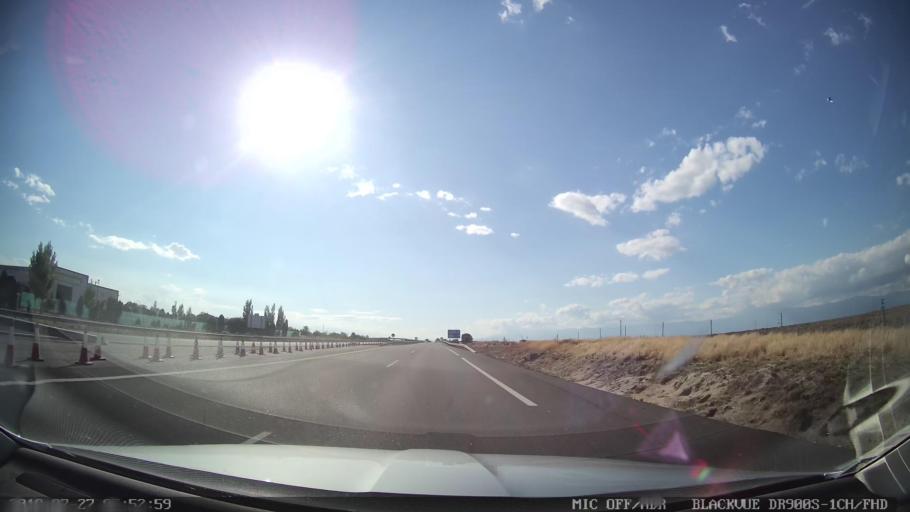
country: ES
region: Castille-La Mancha
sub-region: Province of Toledo
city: Torralba de Oropesa
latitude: 39.9286
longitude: -5.1333
